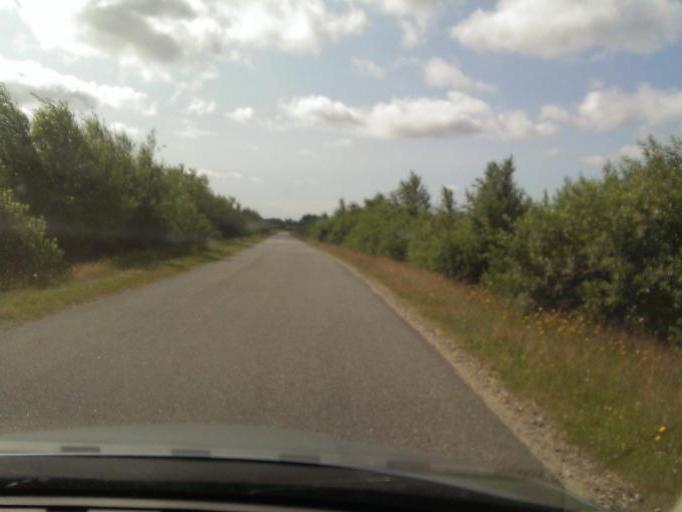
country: DK
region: North Denmark
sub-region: Bronderslev Kommune
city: Bronderslev
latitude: 57.2005
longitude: 9.9280
